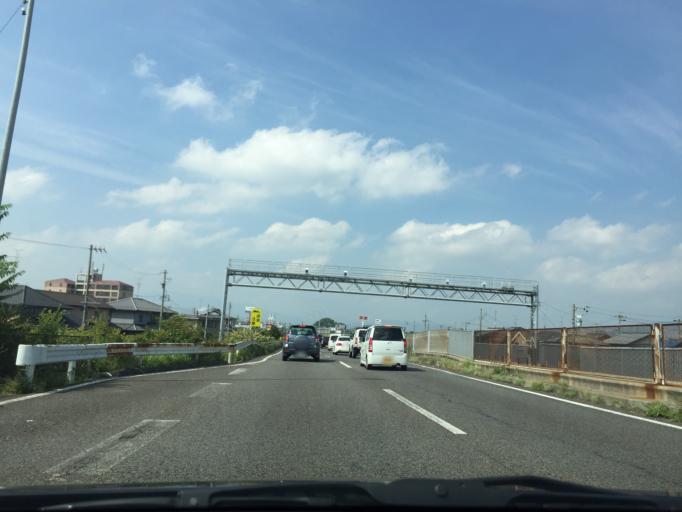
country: JP
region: Gifu
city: Ogaki
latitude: 35.3817
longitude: 136.6747
